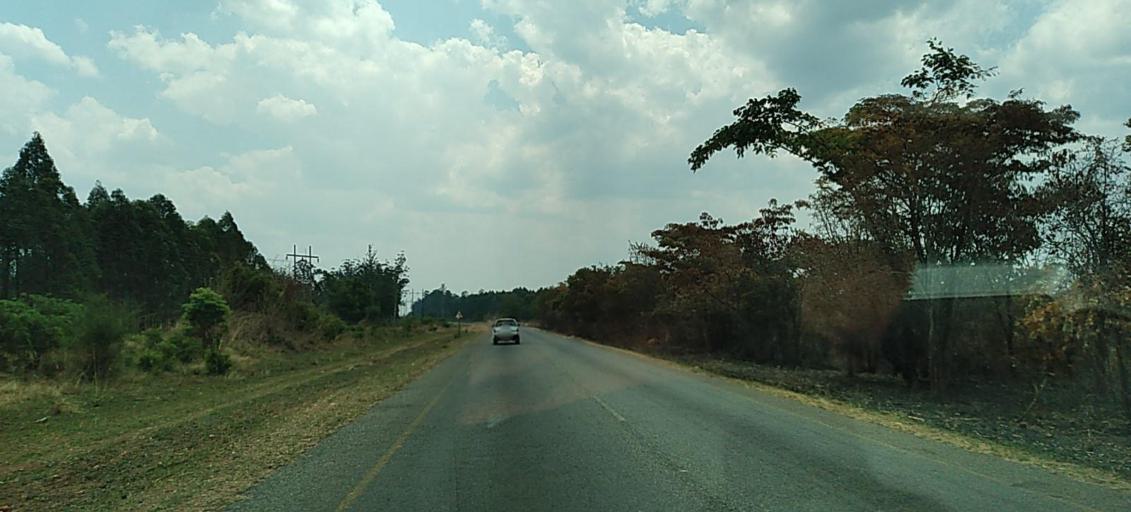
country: ZM
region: Copperbelt
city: Kalulushi
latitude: -12.8378
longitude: 27.9289
